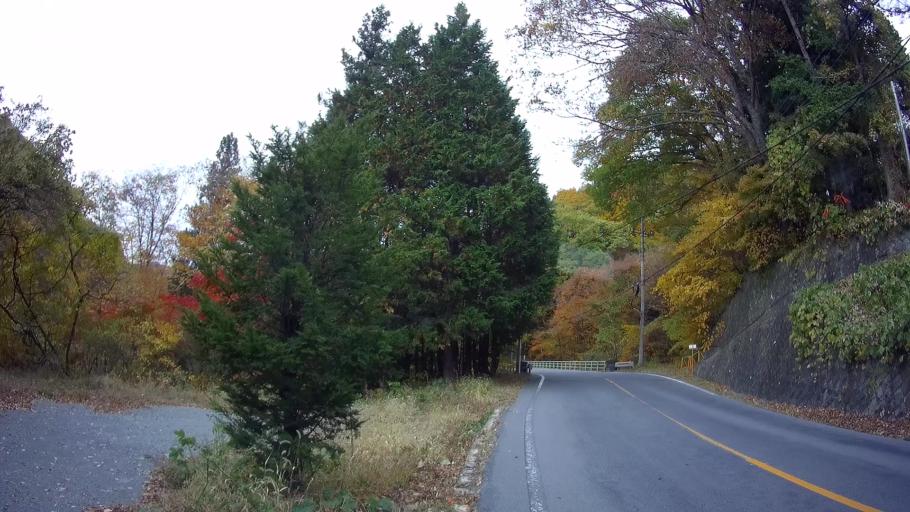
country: JP
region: Gunma
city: Nakanojomachi
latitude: 36.5560
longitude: 138.6475
